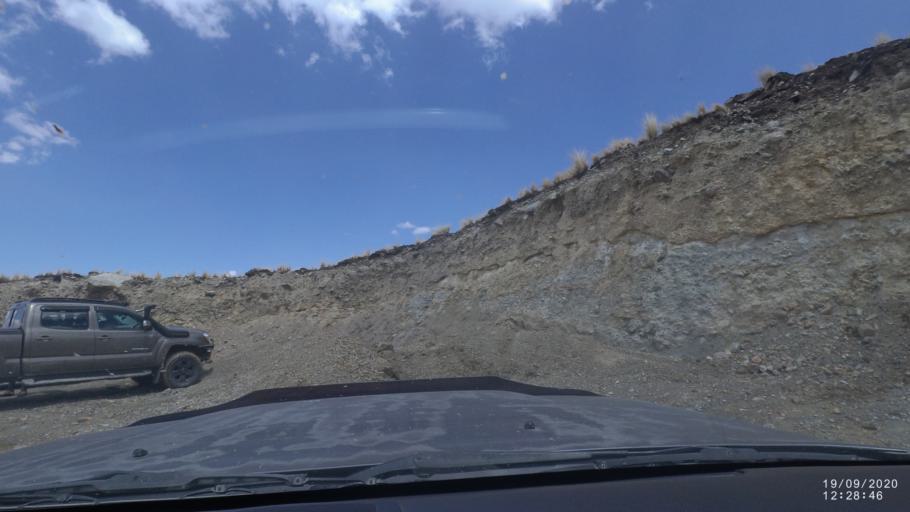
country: BO
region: Cochabamba
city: Cochabamba
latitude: -17.2944
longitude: -66.1140
